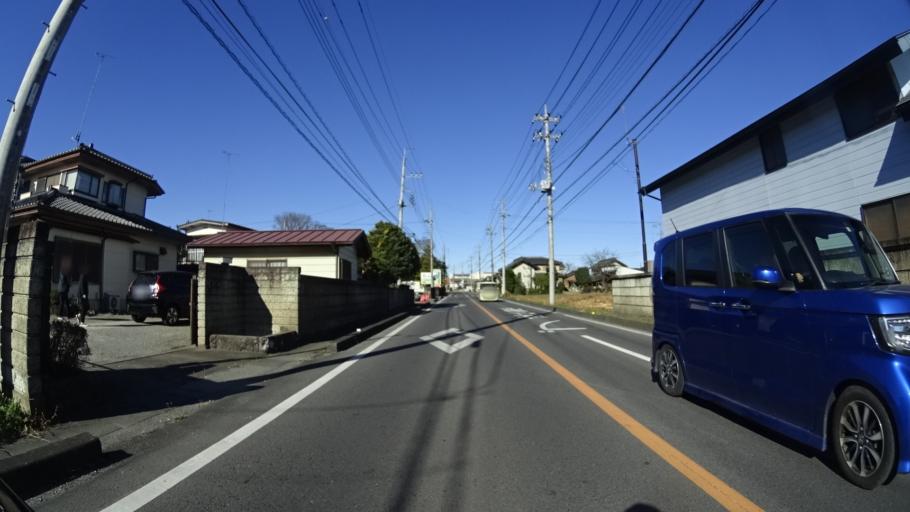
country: JP
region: Tochigi
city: Tochigi
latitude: 36.4247
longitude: 139.7495
